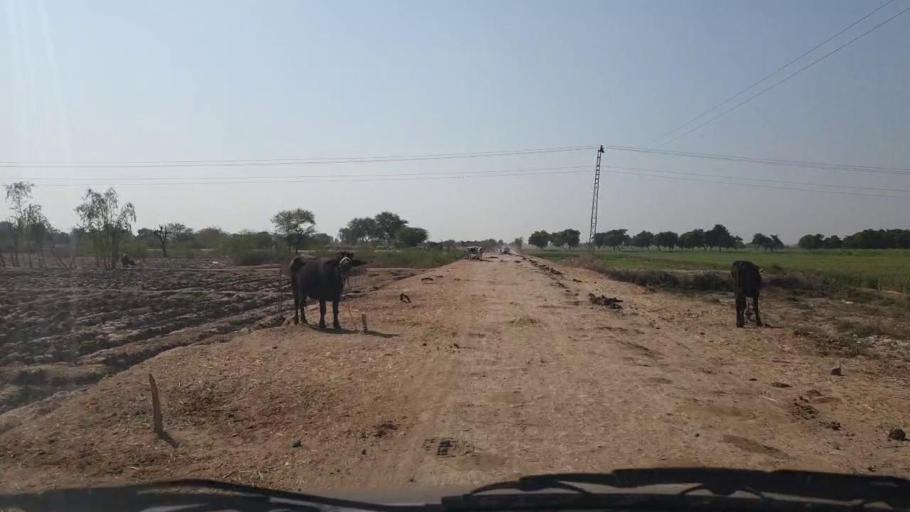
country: PK
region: Sindh
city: Samaro
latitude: 25.2717
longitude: 69.2508
